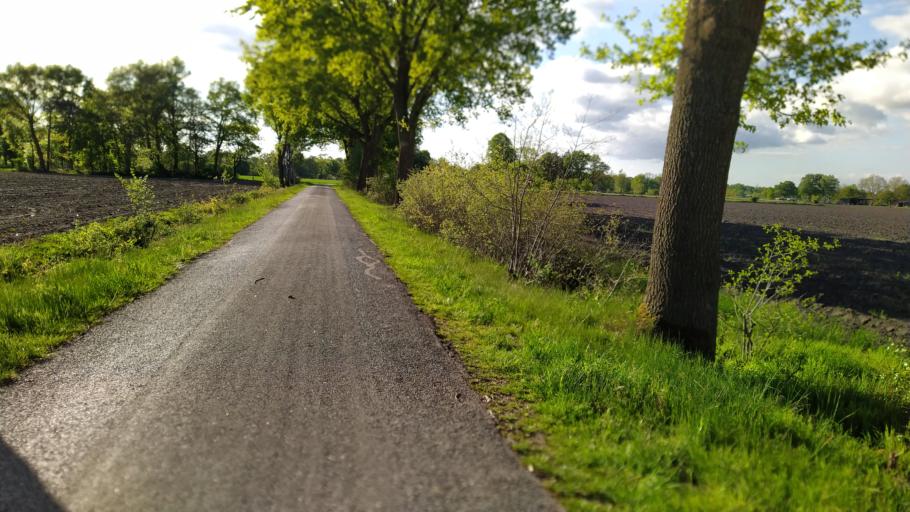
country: DE
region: Lower Saxony
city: Farven
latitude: 53.4059
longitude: 9.3417
